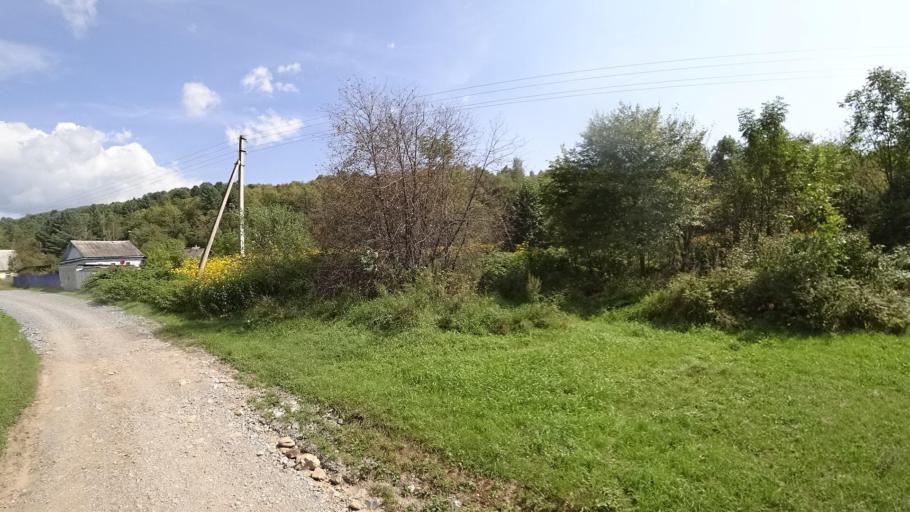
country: RU
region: Jewish Autonomous Oblast
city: Londoko
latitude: 49.0277
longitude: 131.9341
